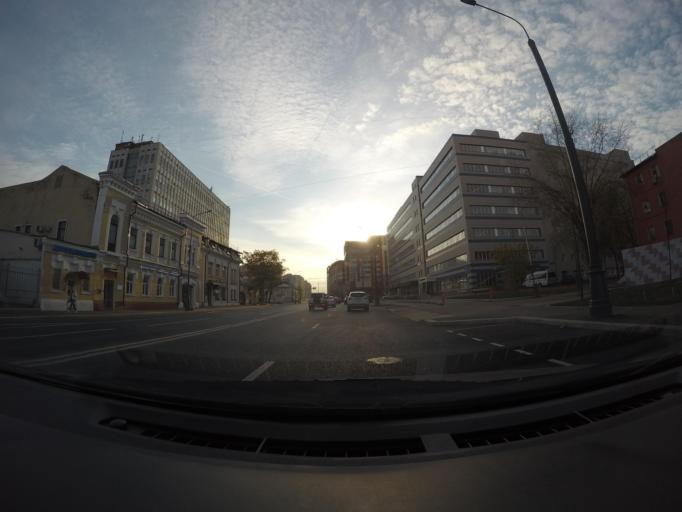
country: RU
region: Moscow
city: Lefortovo
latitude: 55.7802
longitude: 37.6935
